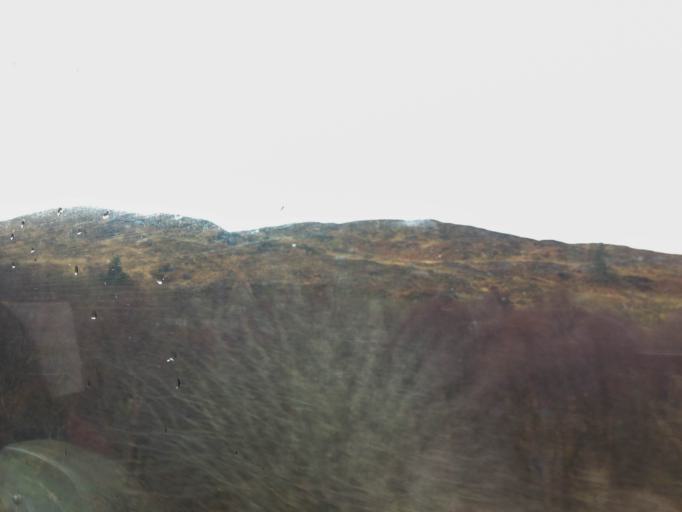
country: GB
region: Scotland
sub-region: Argyll and Bute
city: Isle Of Mull
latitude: 56.9922
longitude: -5.8269
